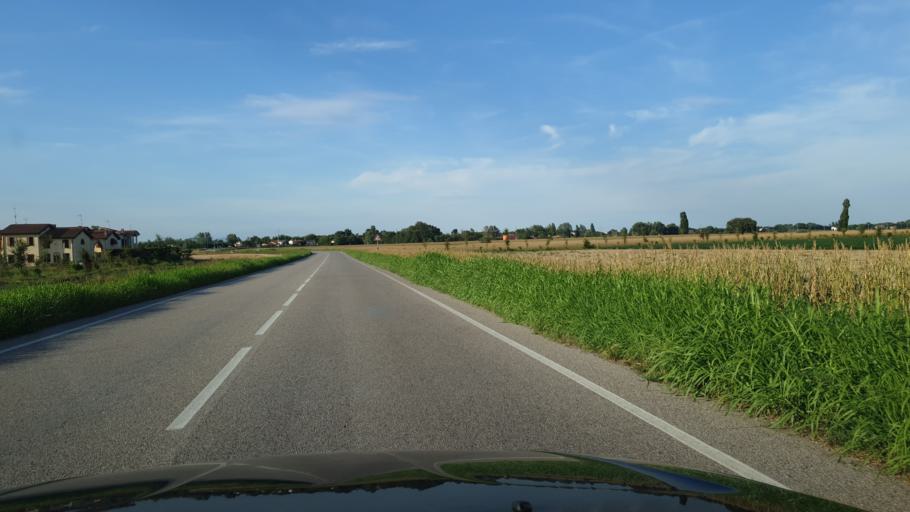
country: IT
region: Veneto
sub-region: Provincia di Rovigo
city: Pincara
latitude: 44.9930
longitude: 11.6152
